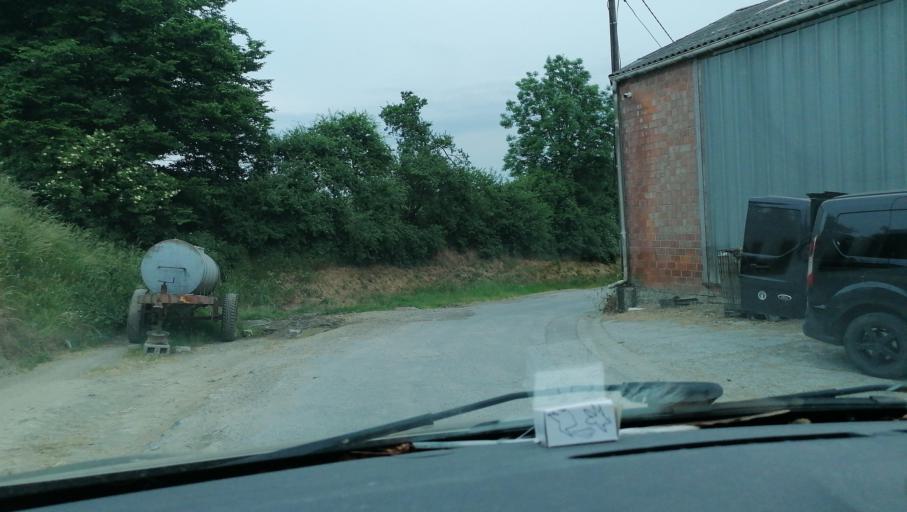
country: BE
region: Wallonia
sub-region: Province du Hainaut
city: Beaumont
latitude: 50.2032
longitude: 4.1686
